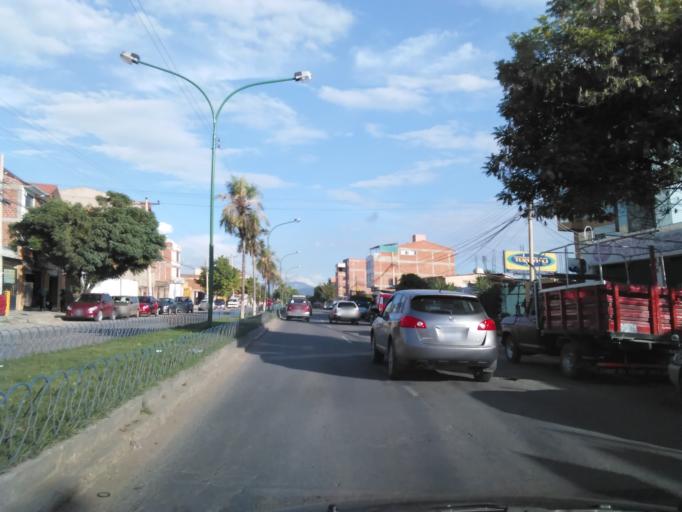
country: BO
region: Cochabamba
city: Cochabamba
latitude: -17.3550
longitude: -66.1871
